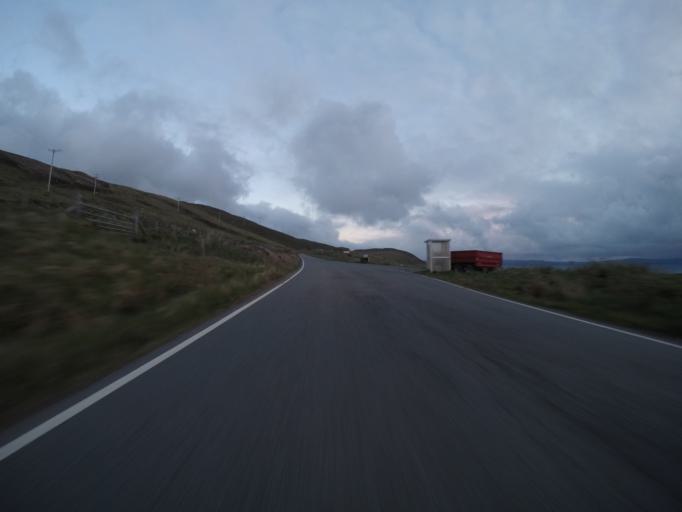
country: GB
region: Scotland
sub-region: Highland
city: Portree
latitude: 57.6101
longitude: -6.3736
